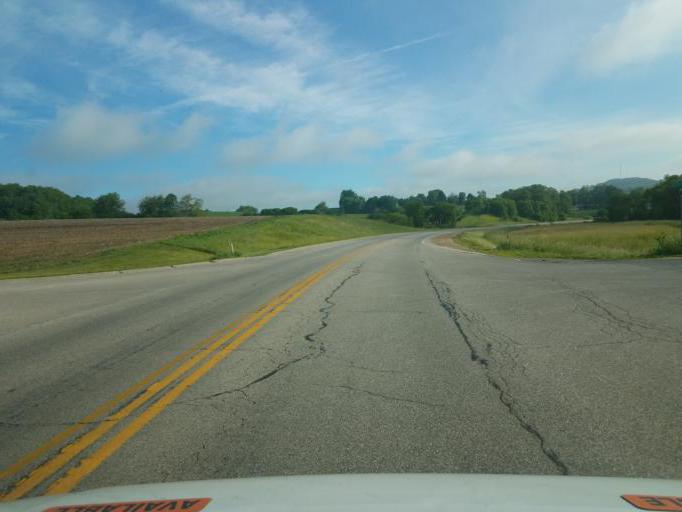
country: US
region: Wisconsin
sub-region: Vernon County
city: Hillsboro
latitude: 43.6437
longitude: -90.3573
